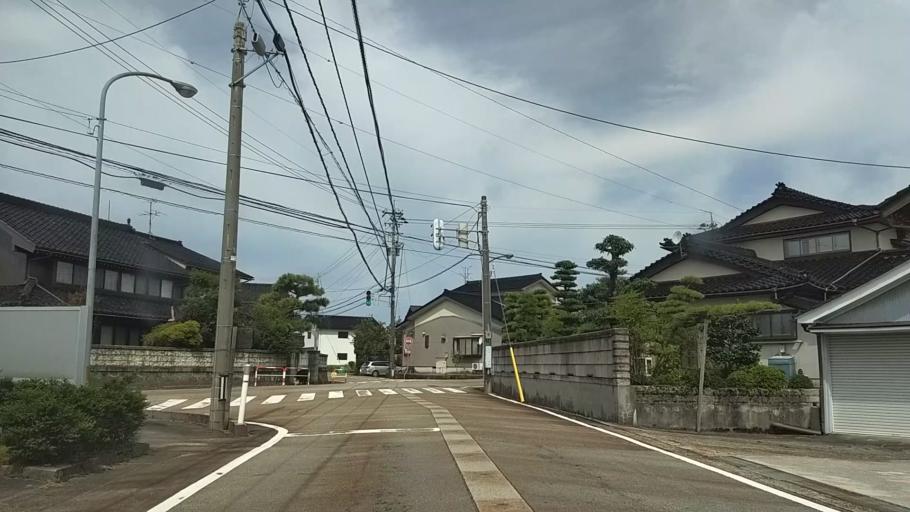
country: JP
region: Toyama
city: Kamiichi
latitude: 36.7398
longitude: 137.3728
